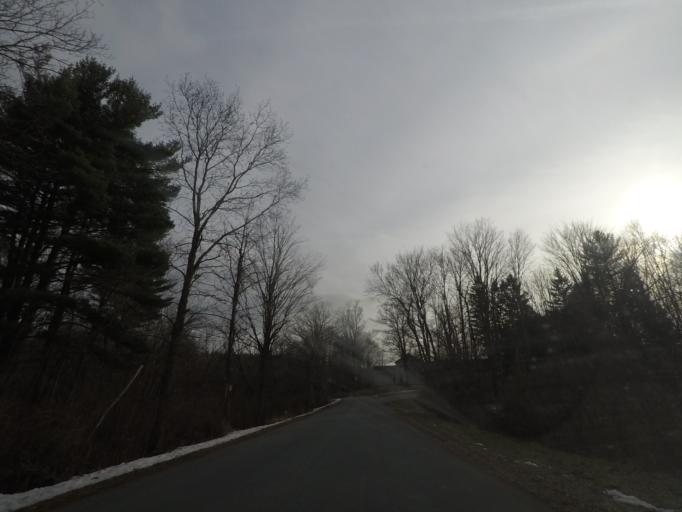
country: US
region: New York
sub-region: Rensselaer County
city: West Sand Lake
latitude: 42.6441
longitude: -73.6528
